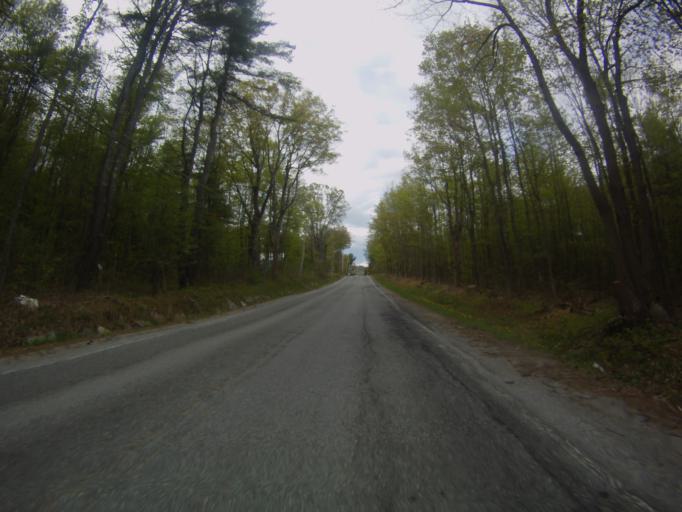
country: US
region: New York
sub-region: Essex County
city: Mineville
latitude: 44.0780
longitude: -73.5278
